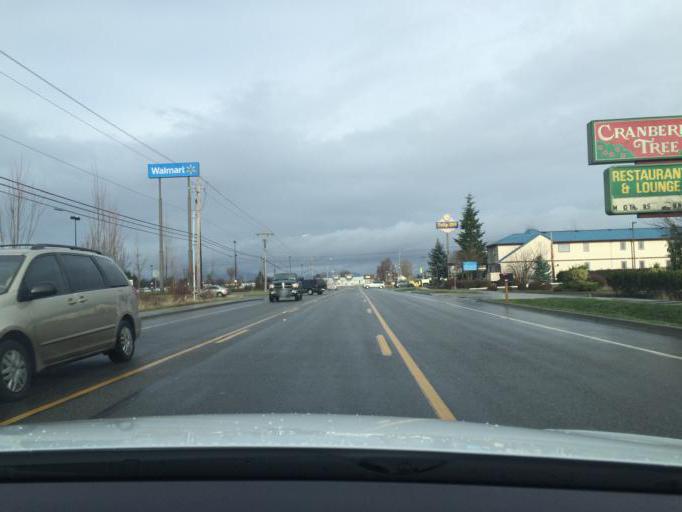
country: US
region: Washington
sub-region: Skagit County
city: Mount Vernon
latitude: 48.4394
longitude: -122.3431
